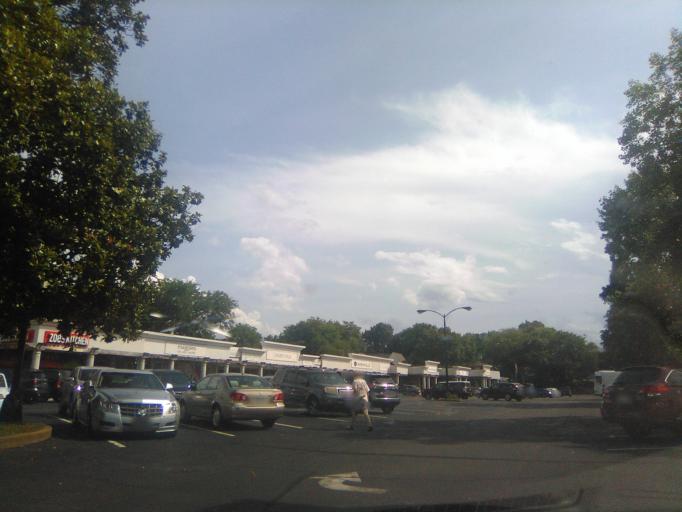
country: US
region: Tennessee
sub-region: Davidson County
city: Belle Meade
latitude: 36.0981
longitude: -86.8722
